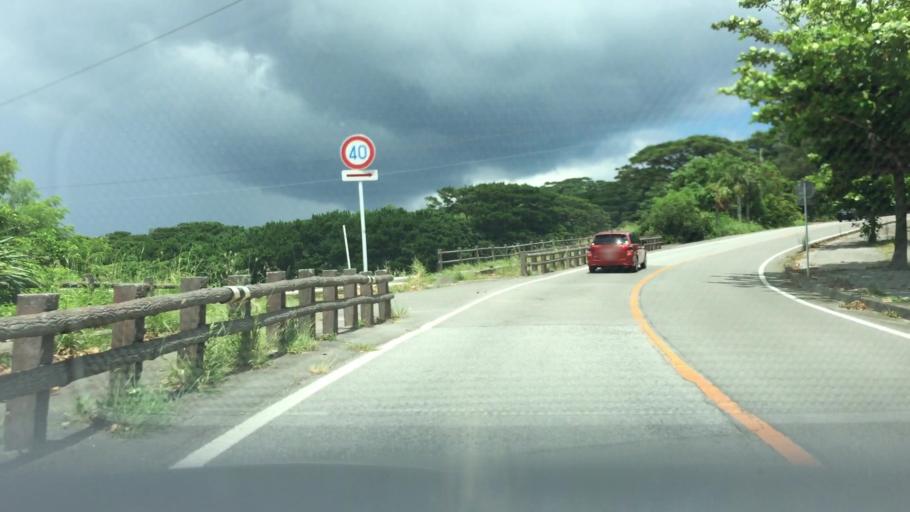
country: JP
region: Okinawa
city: Ishigaki
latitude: 24.4350
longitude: 124.1200
